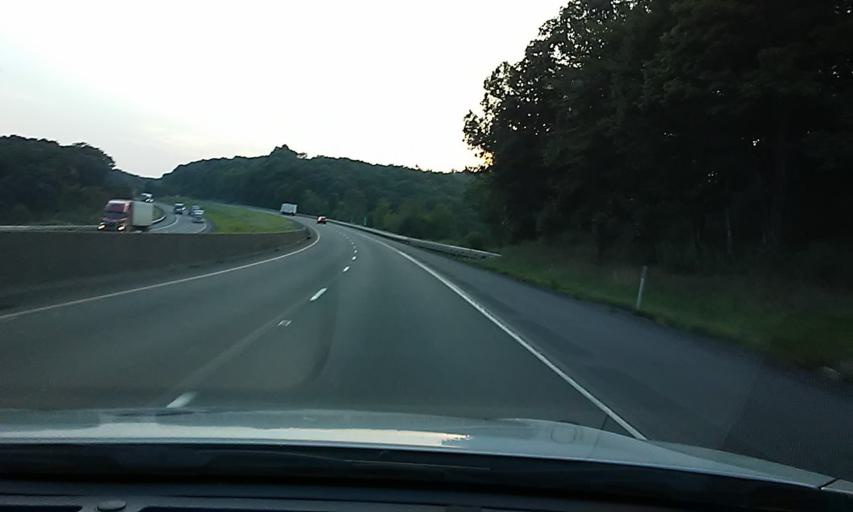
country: US
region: Pennsylvania
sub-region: Clarion County
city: Marianne
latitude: 41.1976
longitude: -79.4674
